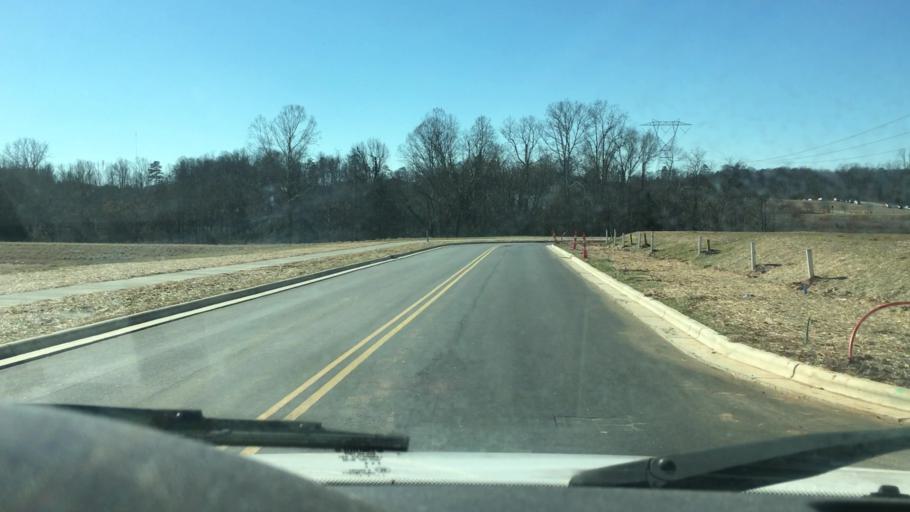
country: US
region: North Carolina
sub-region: Gaston County
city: Davidson
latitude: 35.4748
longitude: -80.8202
